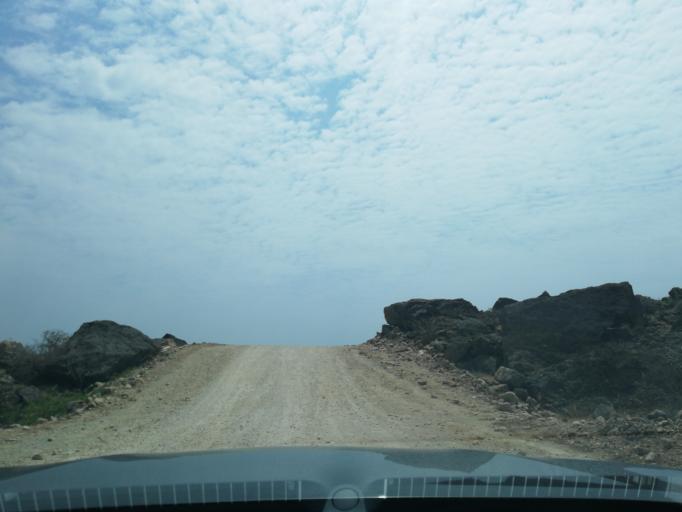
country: OM
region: Zufar
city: Salalah
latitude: 16.8169
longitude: 53.6916
